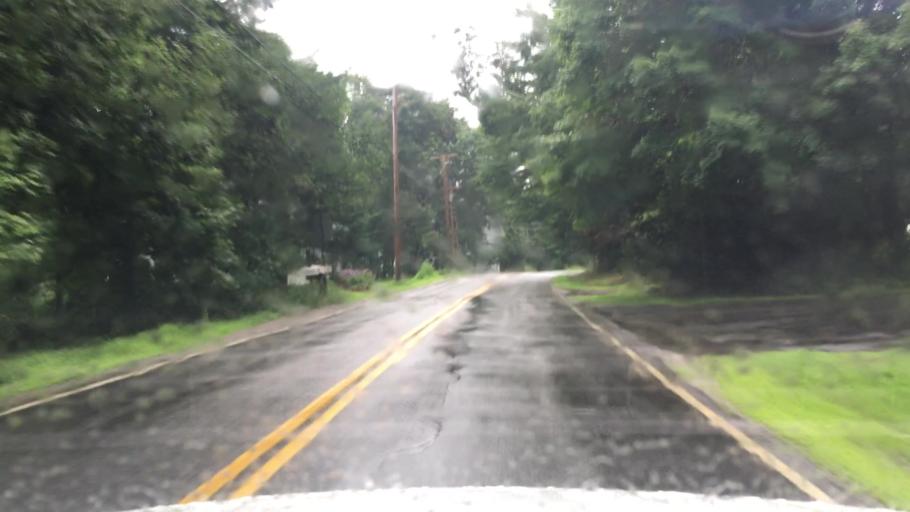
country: US
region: Maine
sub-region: Kennebec County
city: Winthrop
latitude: 44.3050
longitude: -69.9222
